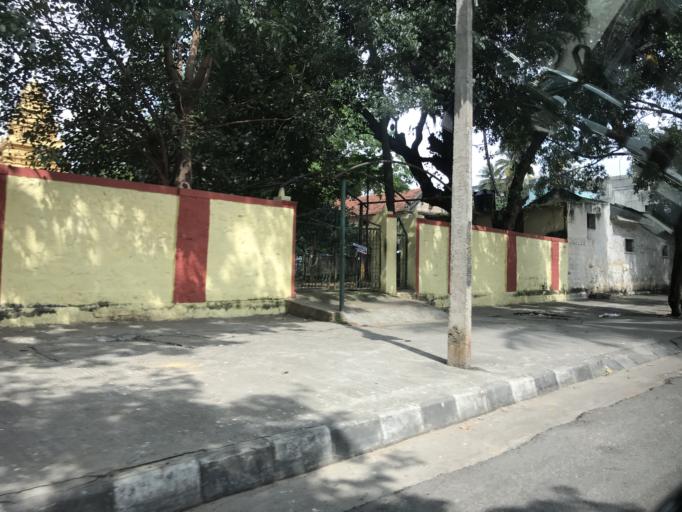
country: IN
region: Karnataka
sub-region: Bangalore Urban
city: Bangalore
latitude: 12.9580
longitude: 77.5696
